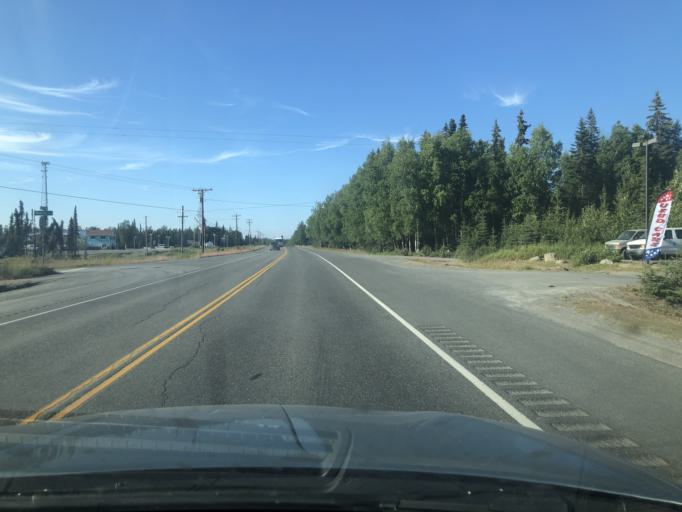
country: US
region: Alaska
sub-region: Kenai Peninsula Borough
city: Ridgeway
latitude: 60.5234
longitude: -151.0812
